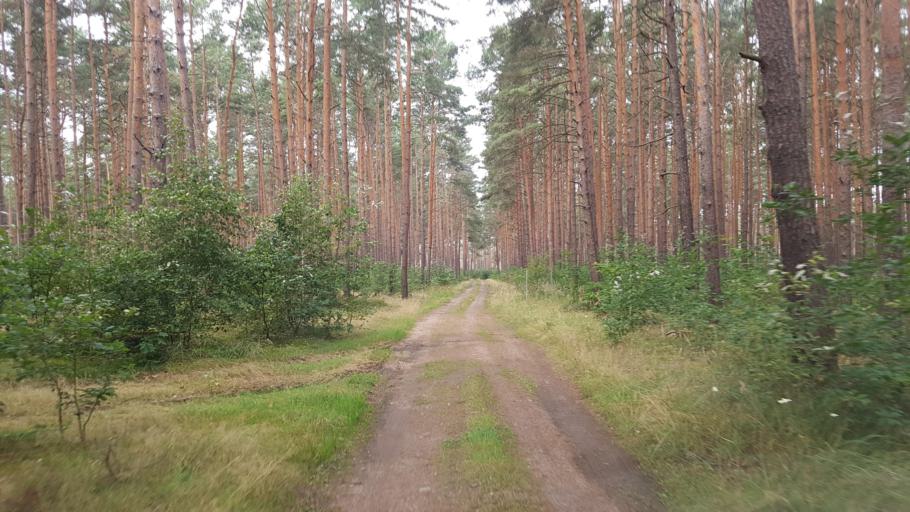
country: DE
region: Brandenburg
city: Hohenbucko
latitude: 51.7871
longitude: 13.5746
